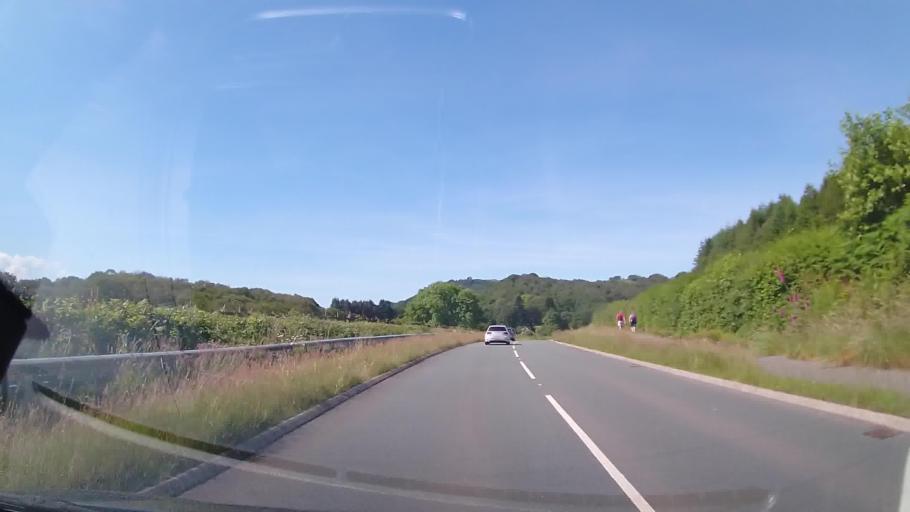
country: GB
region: Wales
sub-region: Sir Powys
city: Machynlleth
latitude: 52.5784
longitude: -3.9444
